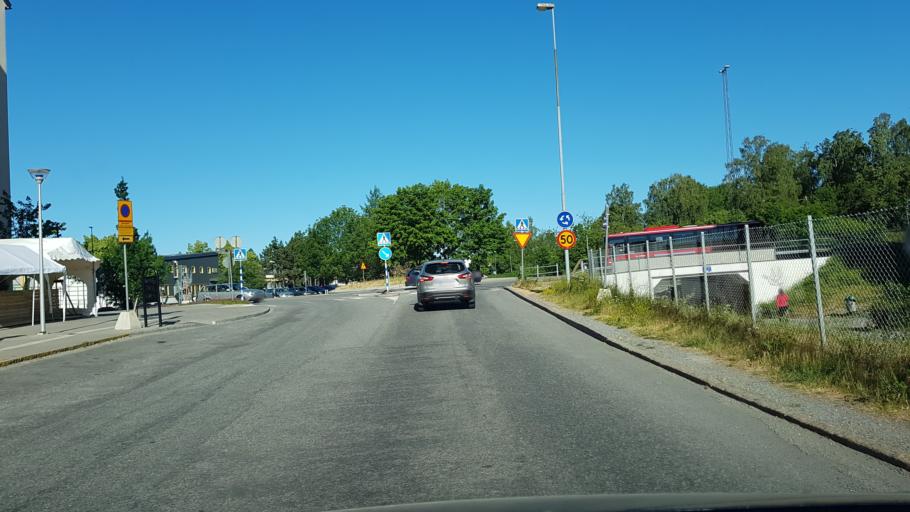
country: SE
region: Stockholm
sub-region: Jarfalla Kommun
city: Jakobsberg
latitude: 59.4181
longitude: 17.8306
